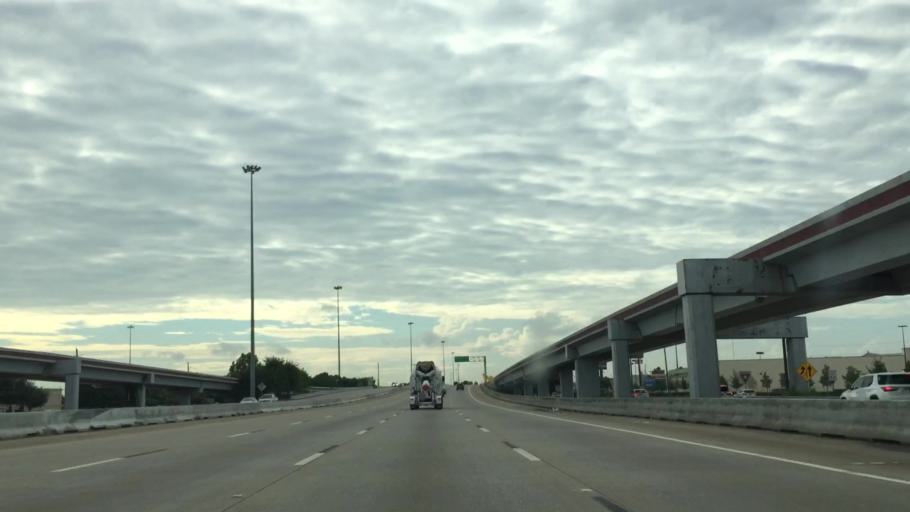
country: US
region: Texas
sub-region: Harris County
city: Jersey Village
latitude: 29.9635
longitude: -95.5511
